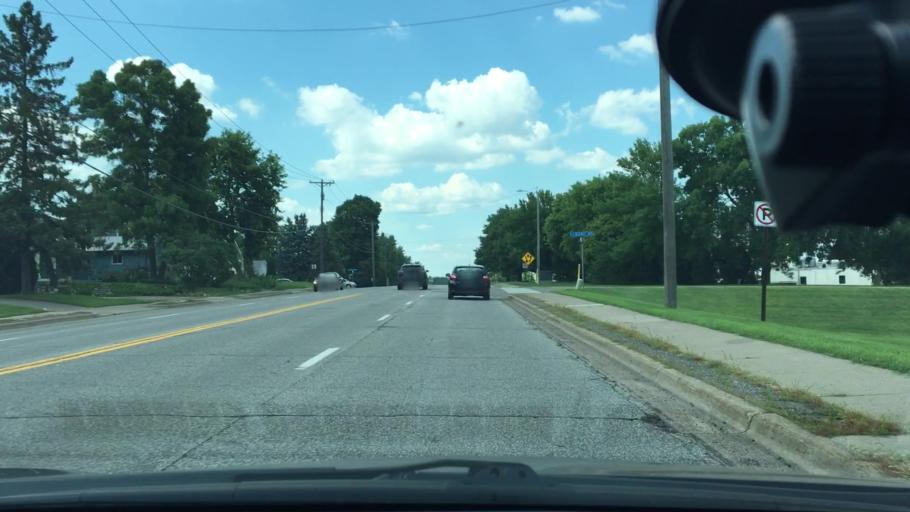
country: US
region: Minnesota
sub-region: Hennepin County
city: New Hope
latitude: 45.0277
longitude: -93.3802
